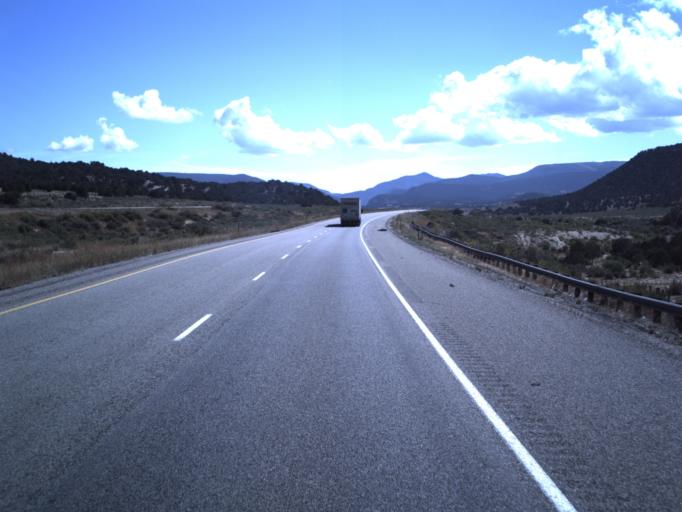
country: US
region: Utah
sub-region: Sevier County
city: Salina
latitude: 38.9244
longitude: -111.7733
